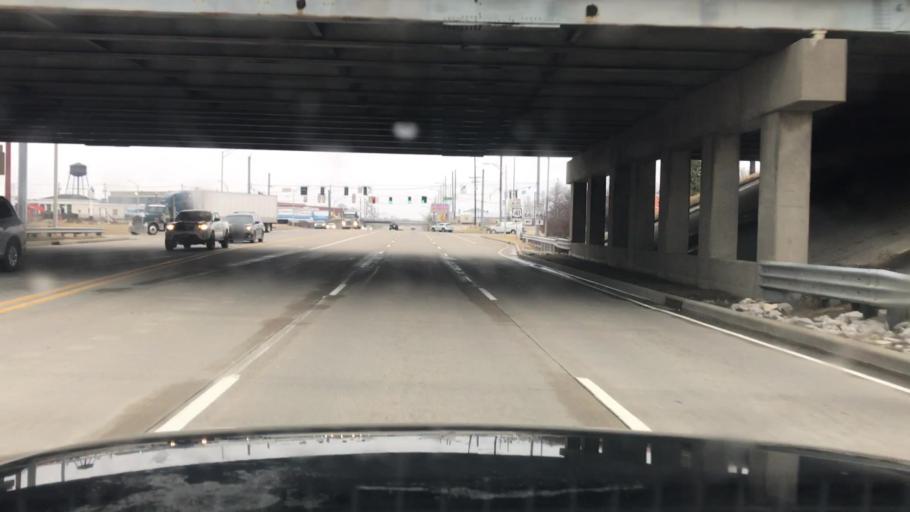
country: US
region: Indiana
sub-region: Vanderburgh County
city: Evansville
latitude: 37.9991
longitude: -87.5374
